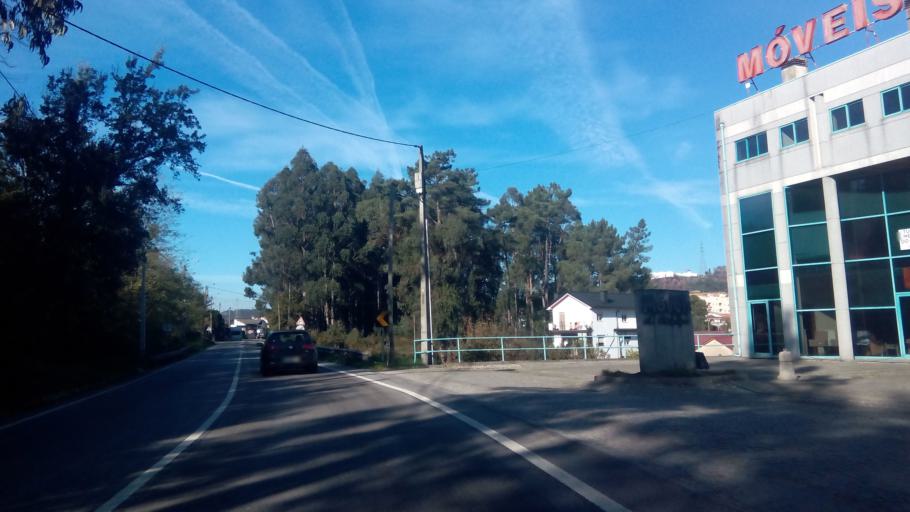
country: PT
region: Porto
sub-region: Paredes
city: Gandra
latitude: 41.1918
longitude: -8.4354
